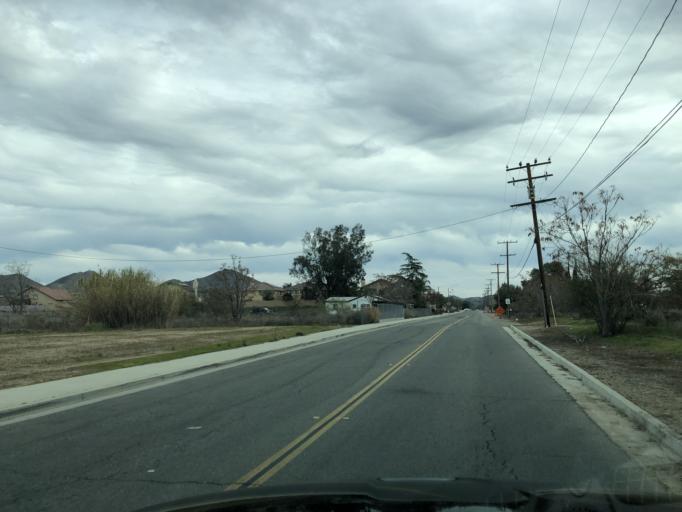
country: US
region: California
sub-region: Riverside County
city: Sedco Hills
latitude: 33.6232
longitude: -117.2899
